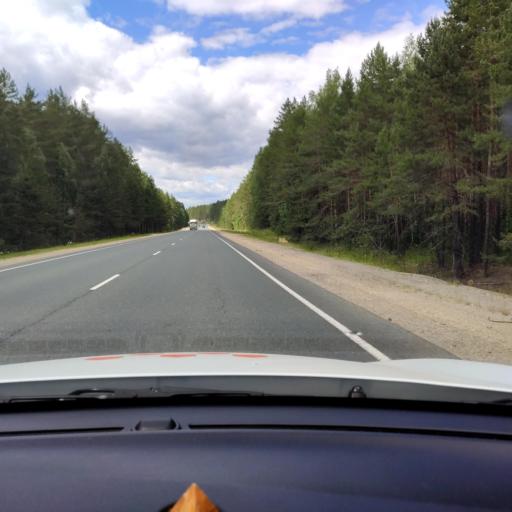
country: RU
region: Mariy-El
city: Pomary
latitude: 56.0545
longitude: 48.3732
